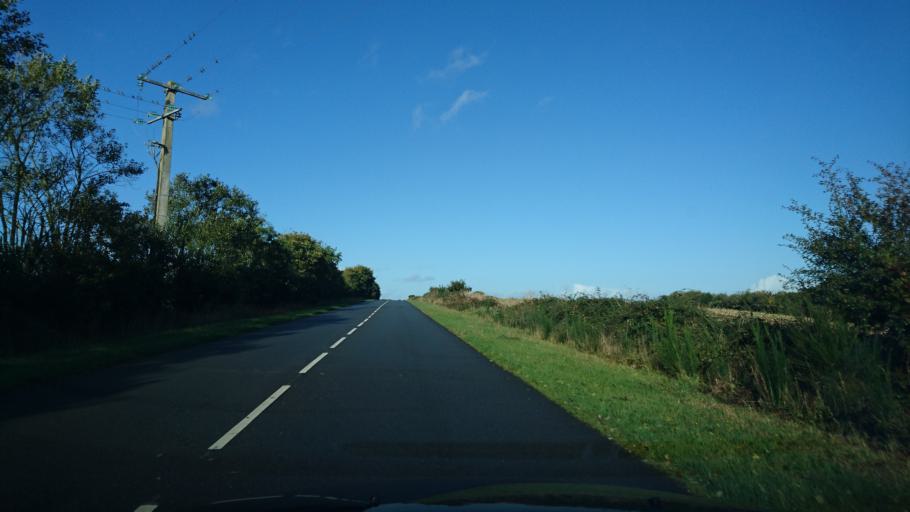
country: FR
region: Brittany
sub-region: Departement du Finistere
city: Plouarzel
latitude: 48.4389
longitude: -4.7331
